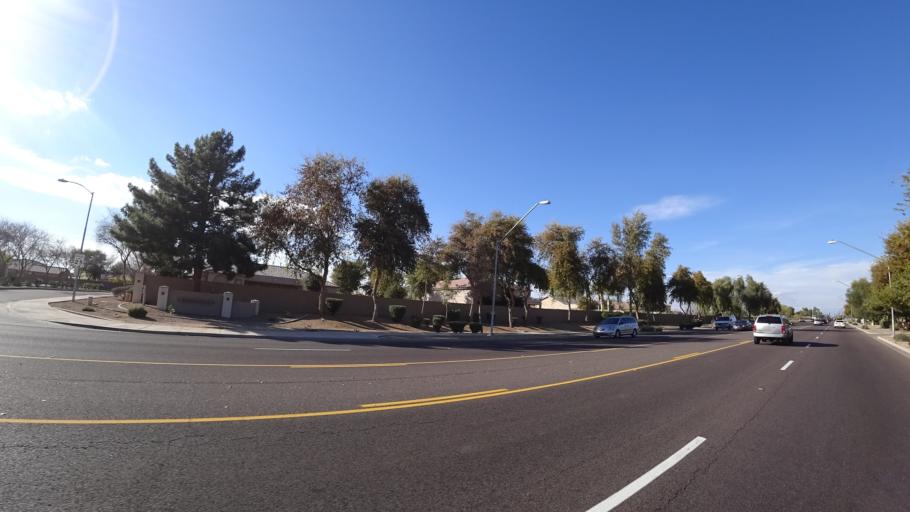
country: US
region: Arizona
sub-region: Maricopa County
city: Glendale
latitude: 33.5178
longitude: -112.2376
